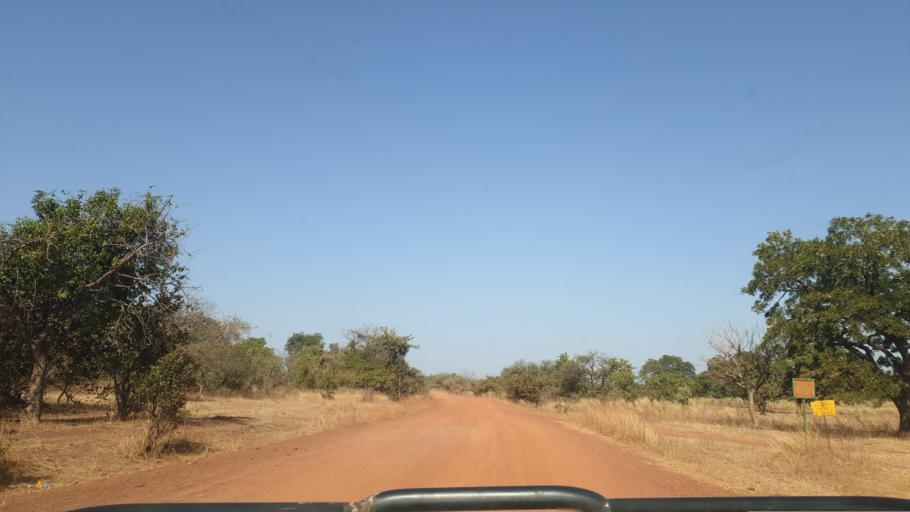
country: ML
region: Sikasso
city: Bougouni
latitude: 11.8161
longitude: -6.9375
